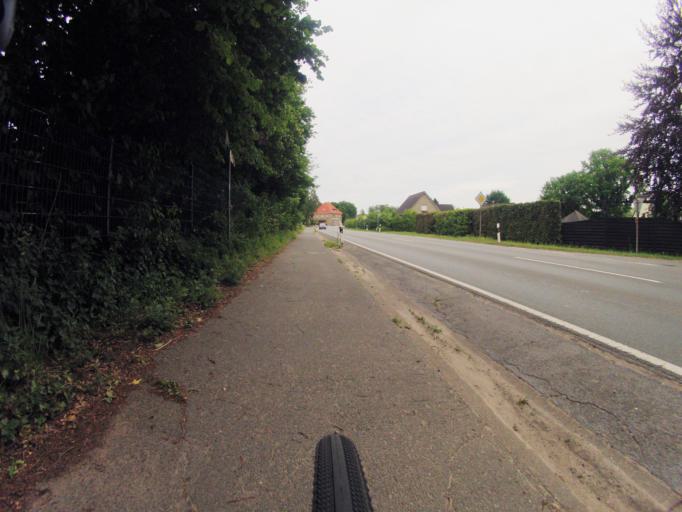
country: DE
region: North Rhine-Westphalia
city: Ibbenburen
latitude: 52.3132
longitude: 7.6618
